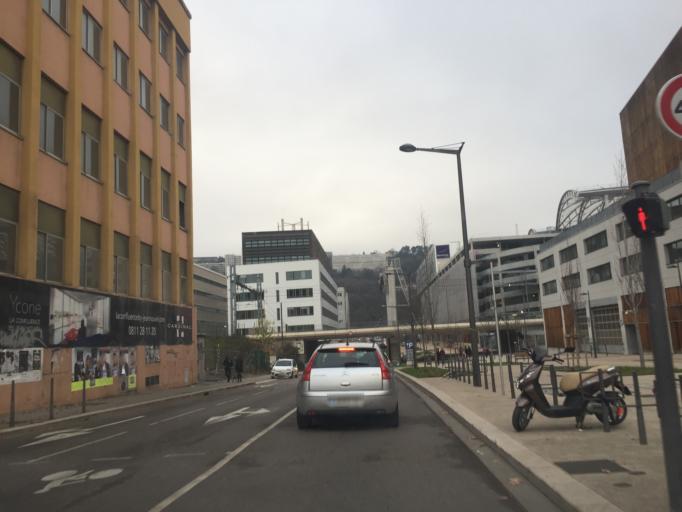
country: FR
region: Rhone-Alpes
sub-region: Departement du Rhone
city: La Mulatiere
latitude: 45.7398
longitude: 4.8181
